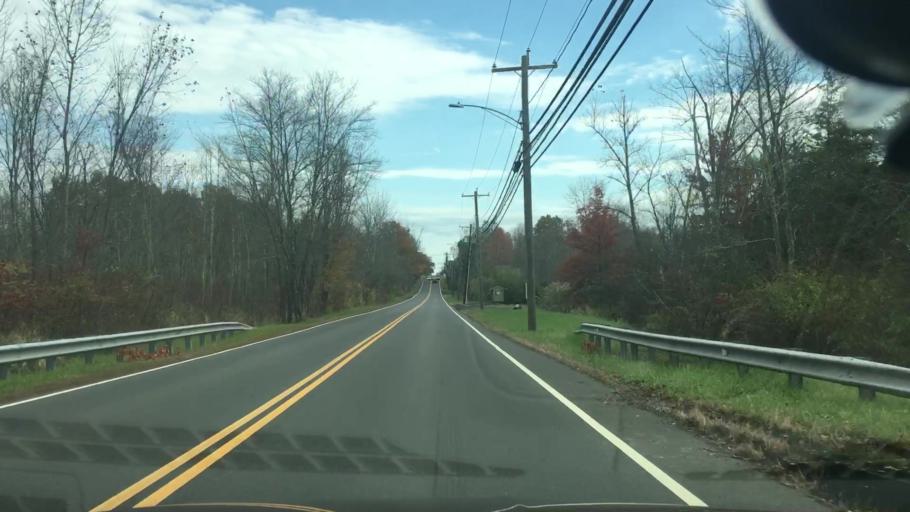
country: US
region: Connecticut
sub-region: Hartford County
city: Kensington
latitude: 41.6159
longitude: -72.7333
